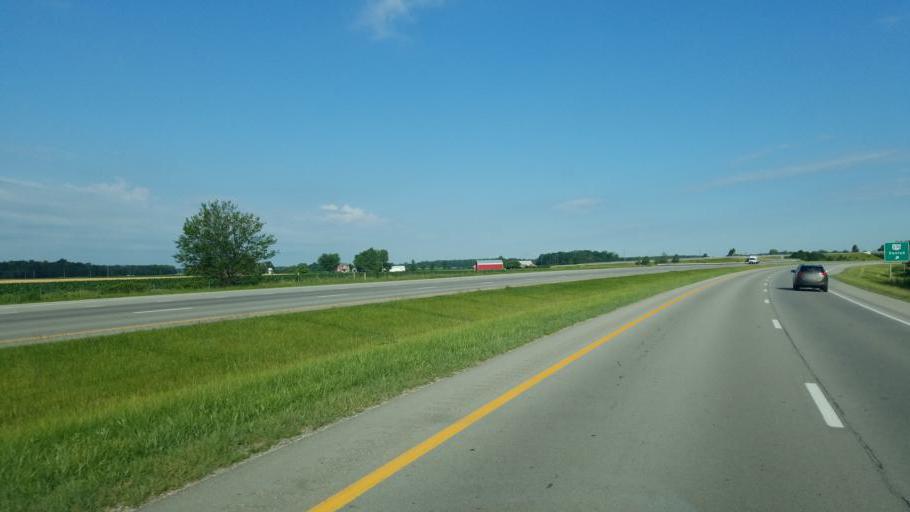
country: US
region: Ohio
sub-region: Wyandot County
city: Carey
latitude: 40.9661
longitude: -83.4788
